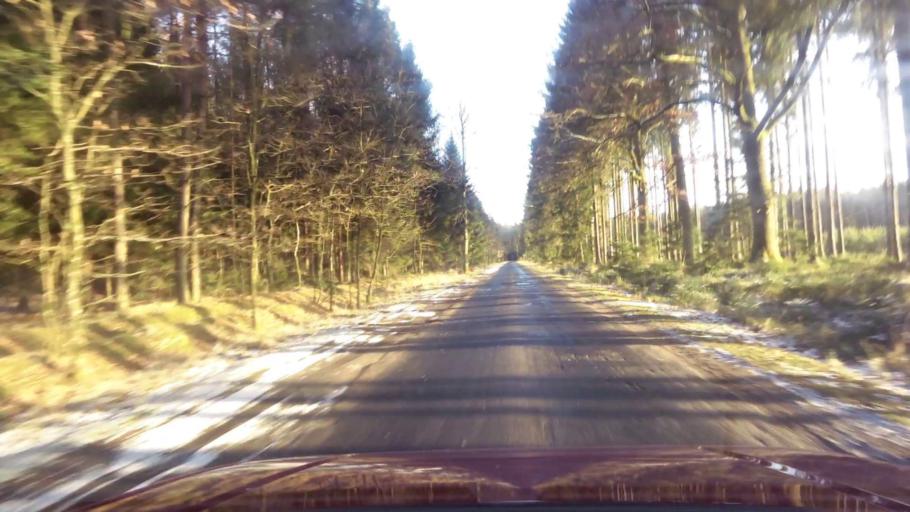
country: PL
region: West Pomeranian Voivodeship
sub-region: Powiat bialogardzki
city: Bialogard
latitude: 54.0999
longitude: 16.0450
